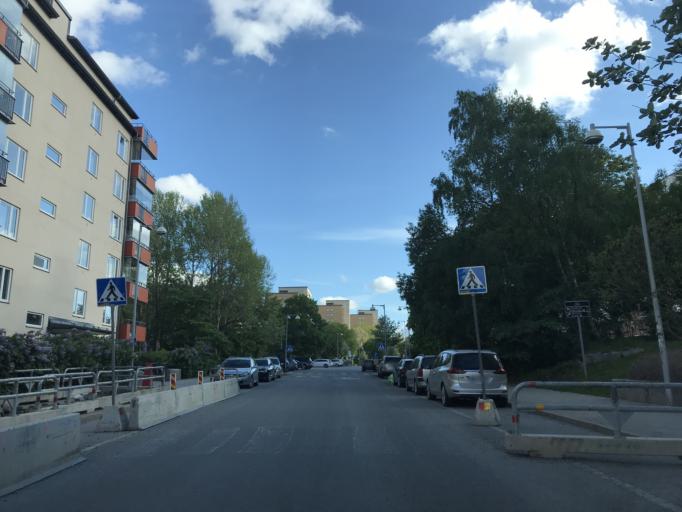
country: SE
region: Stockholm
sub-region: Solna Kommun
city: Solna
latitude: 59.3505
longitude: 17.9966
